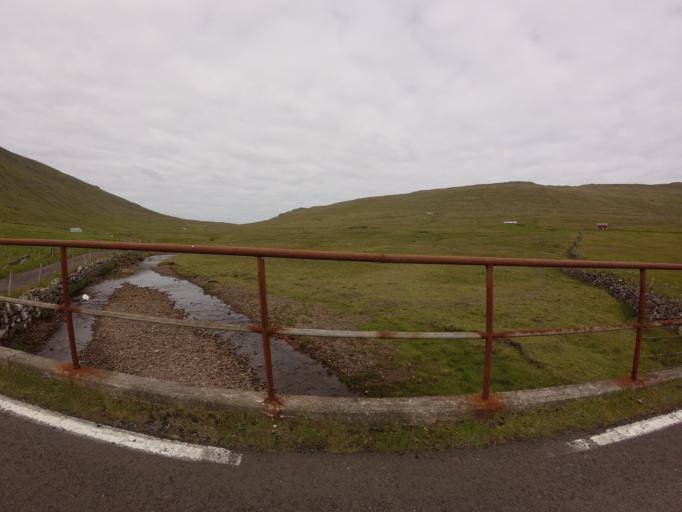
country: FO
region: Suduroy
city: Tvoroyri
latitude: 61.6275
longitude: -6.9423
